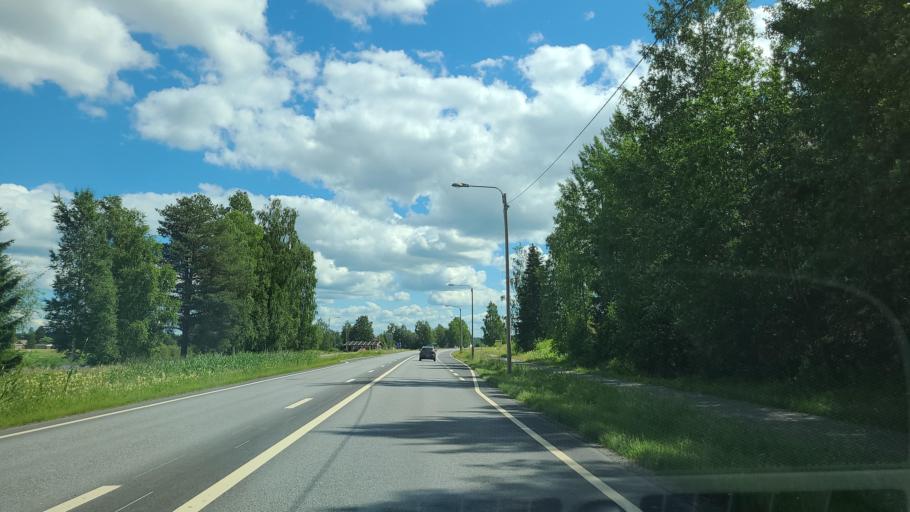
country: FI
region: Ostrobothnia
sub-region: Kyroenmaa
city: Isokyroe
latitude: 62.9741
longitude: 22.3751
